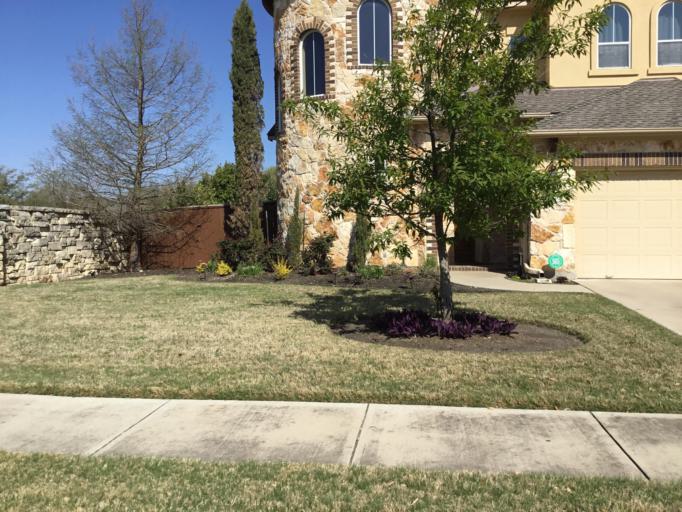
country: US
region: Texas
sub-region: Williamson County
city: Brushy Creek
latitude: 30.5711
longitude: -97.7771
